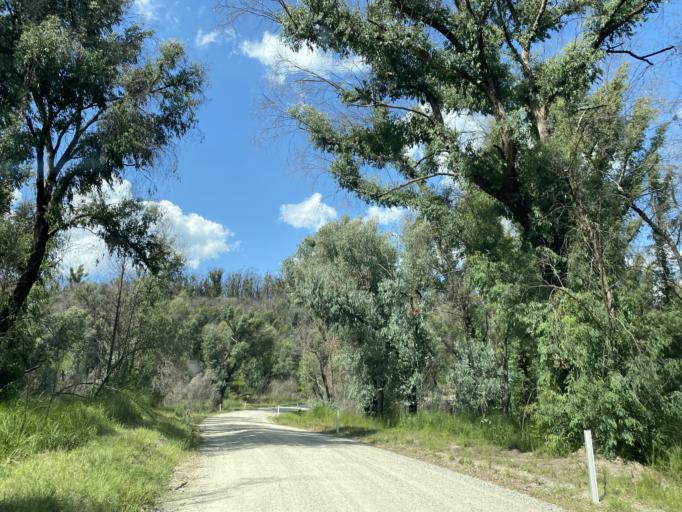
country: AU
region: Victoria
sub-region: Cardinia
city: Bunyip
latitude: -38.0026
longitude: 145.7359
